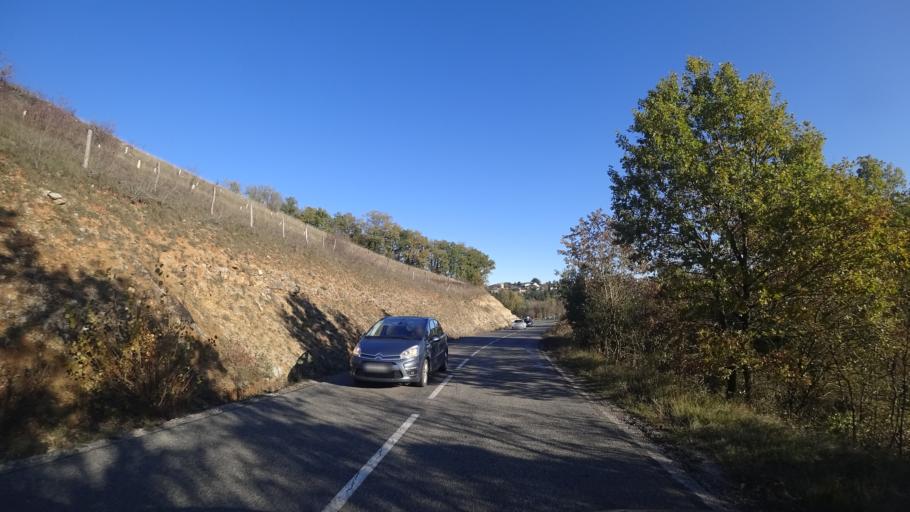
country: FR
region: Midi-Pyrenees
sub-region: Departement de l'Aveyron
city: Rodez
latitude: 44.3793
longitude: 2.5611
